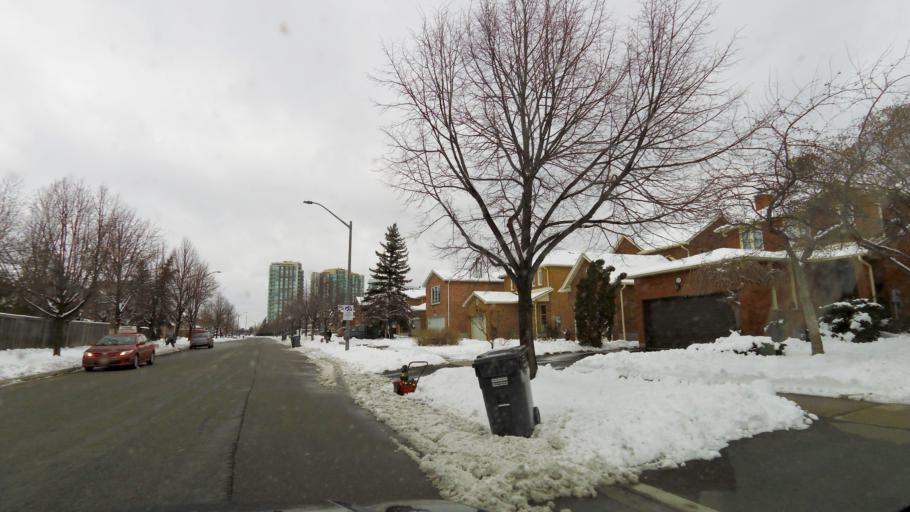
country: CA
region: Ontario
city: Mississauga
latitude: 43.5485
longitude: -79.7133
